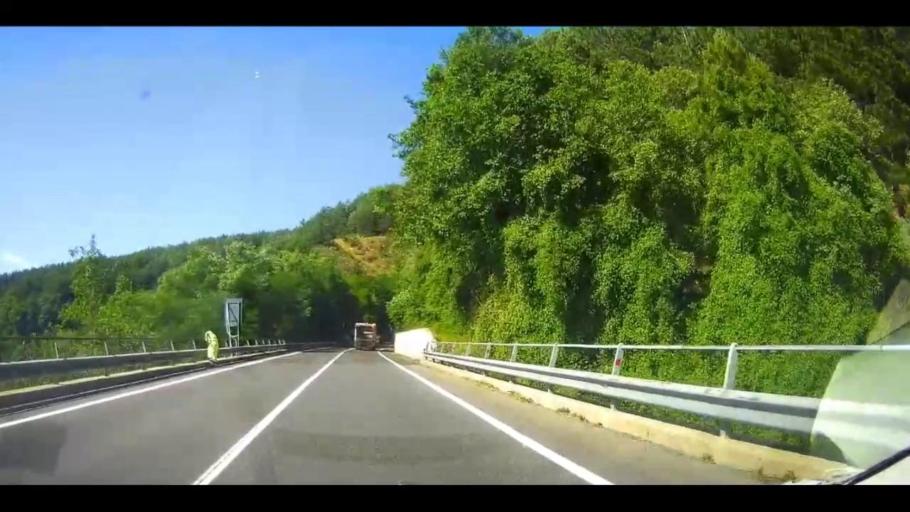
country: IT
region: Calabria
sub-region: Provincia di Cosenza
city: Celico
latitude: 39.3342
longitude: 16.3598
